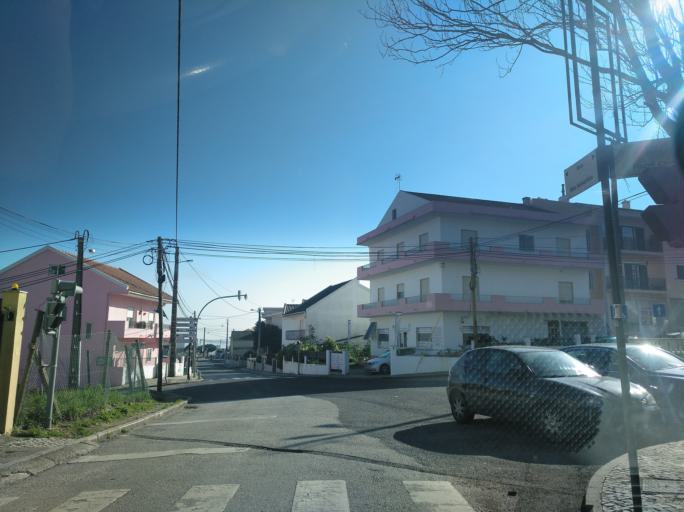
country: PT
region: Lisbon
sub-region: Odivelas
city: Famoes
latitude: 38.7976
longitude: -9.2175
